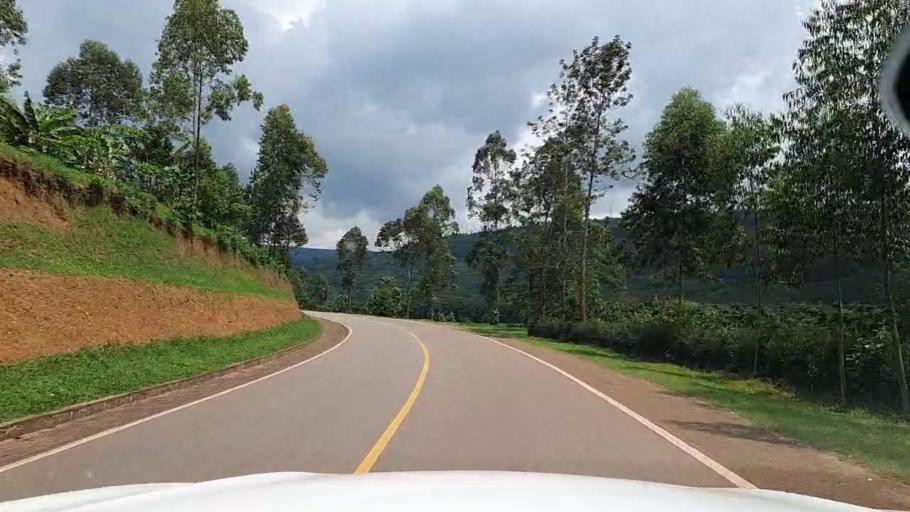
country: RW
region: Kigali
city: Kigali
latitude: -1.8027
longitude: 30.1279
